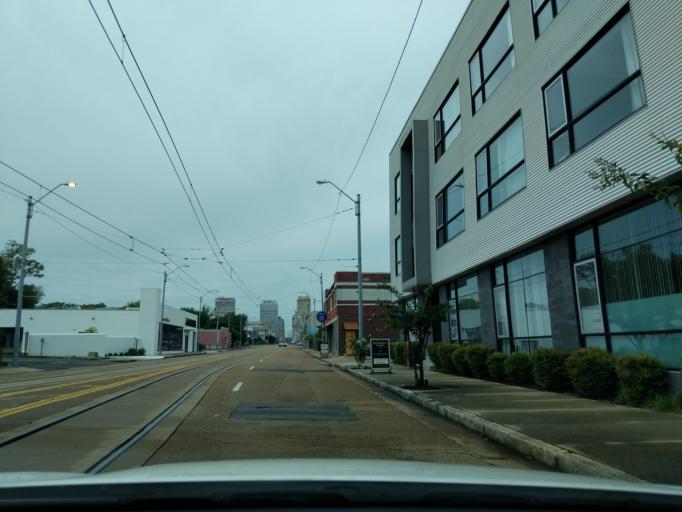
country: US
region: Tennessee
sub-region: Shelby County
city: Memphis
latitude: 35.1414
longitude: -90.0385
